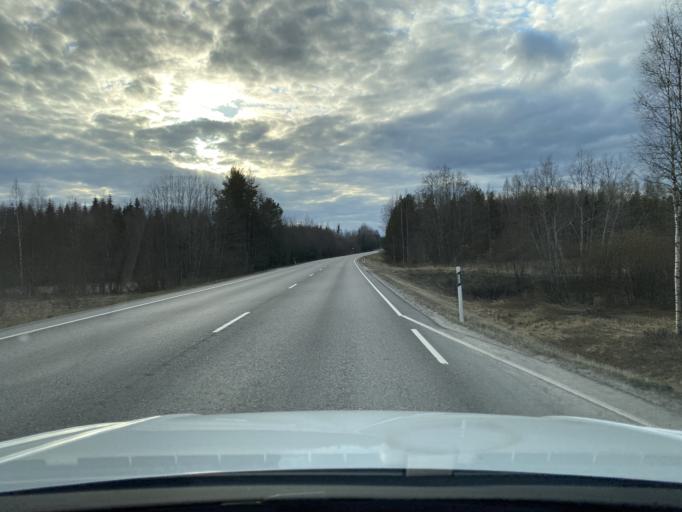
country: FI
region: Haeme
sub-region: Haemeenlinna
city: Renko
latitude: 60.7868
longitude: 24.1376
